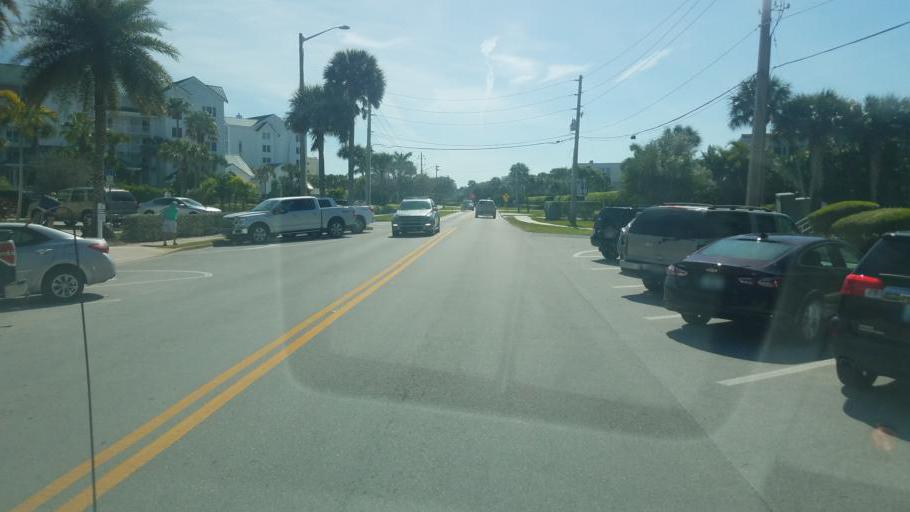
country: US
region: Florida
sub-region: Indian River County
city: Vero Beach
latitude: 27.6480
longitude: -80.3550
